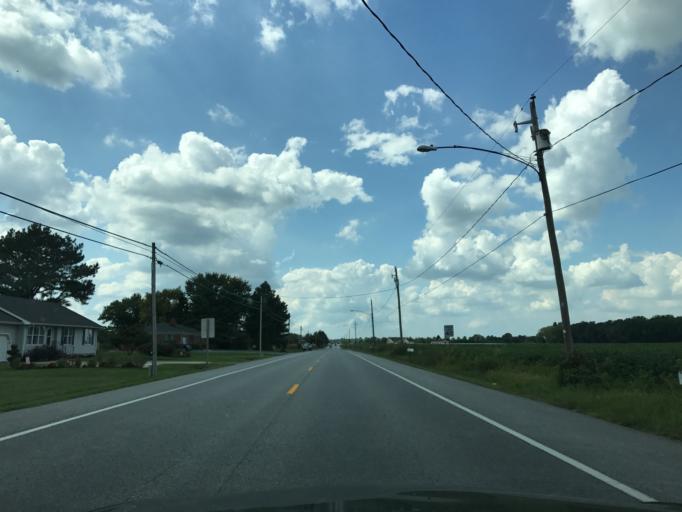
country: US
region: Maryland
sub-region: Queen Anne's County
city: Kingstown
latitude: 39.1862
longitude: -75.8641
